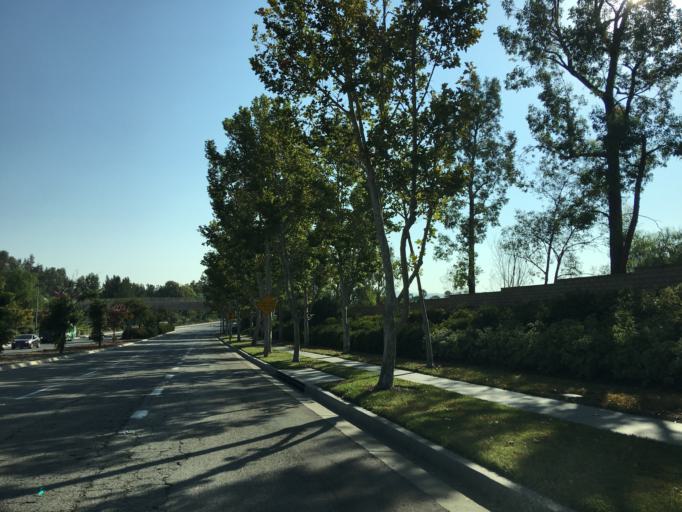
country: US
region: California
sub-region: Los Angeles County
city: Valencia
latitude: 34.4534
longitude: -118.6231
